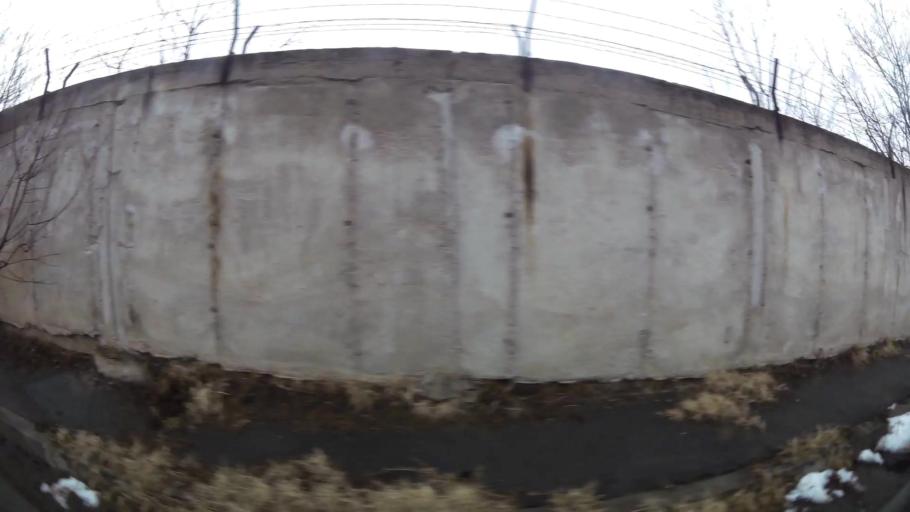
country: RO
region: Ilfov
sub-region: Comuna Mogosoaia
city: Mogosoaia
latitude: 44.5147
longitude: 26.0276
